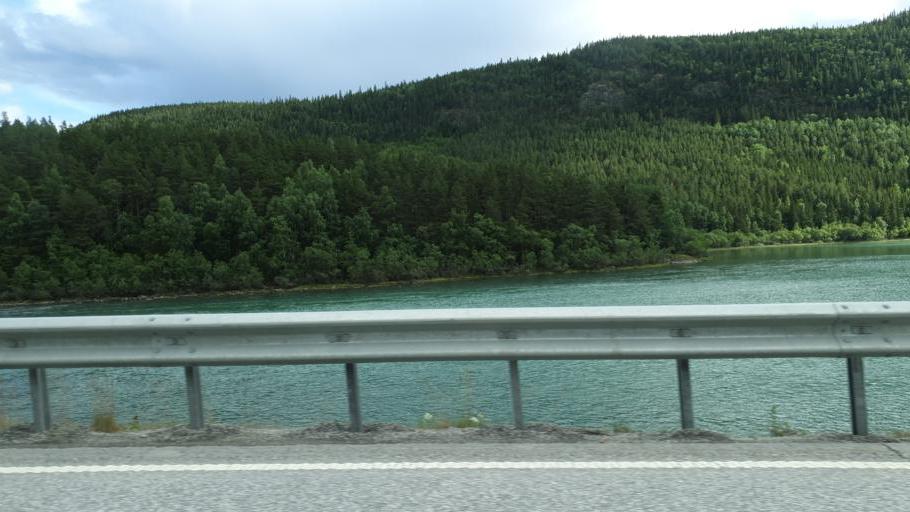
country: NO
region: Oppland
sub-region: Vaga
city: Vagamo
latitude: 61.8740
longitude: 9.1781
